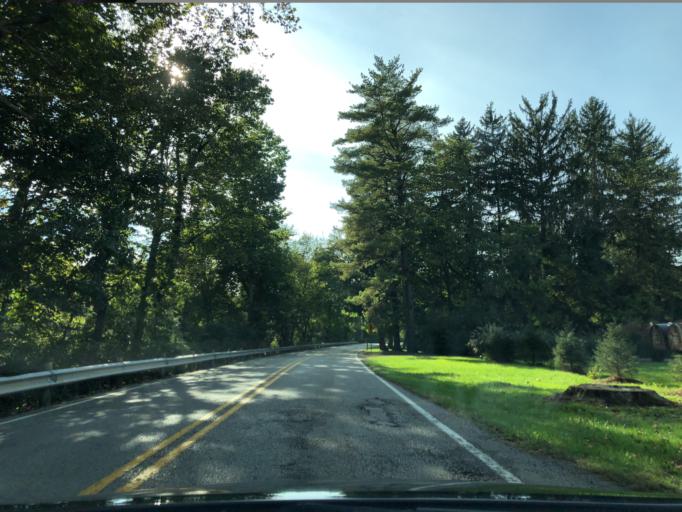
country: US
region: Ohio
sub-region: Hamilton County
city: The Village of Indian Hill
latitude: 39.2518
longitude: -84.2849
